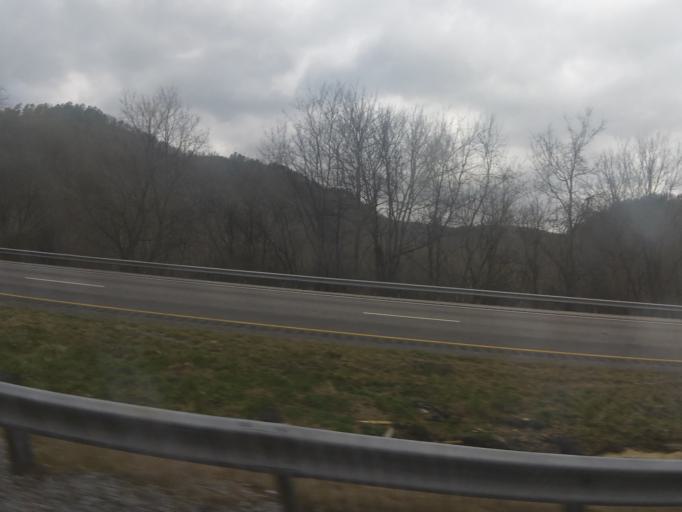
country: US
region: Georgia
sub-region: Dade County
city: Trenton
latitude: 34.9912
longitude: -85.4860
